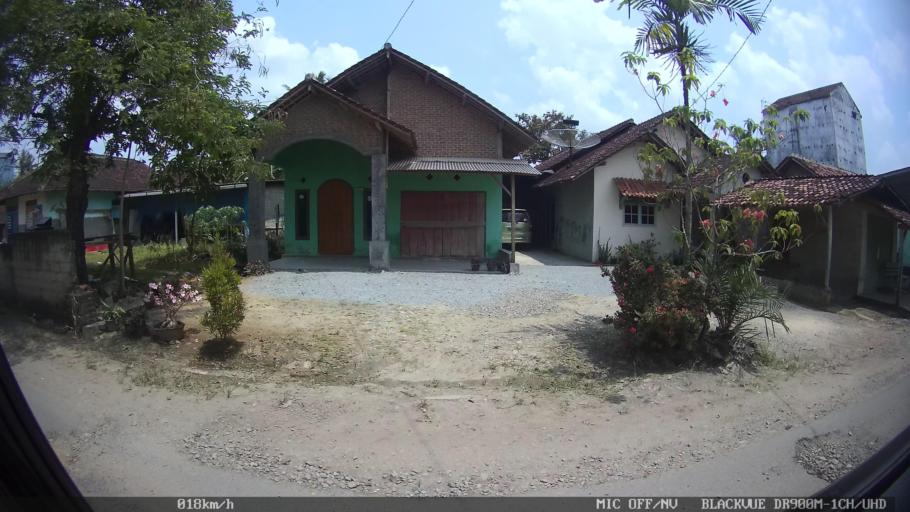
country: ID
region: Lampung
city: Pringsewu
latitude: -5.3585
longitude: 104.9955
